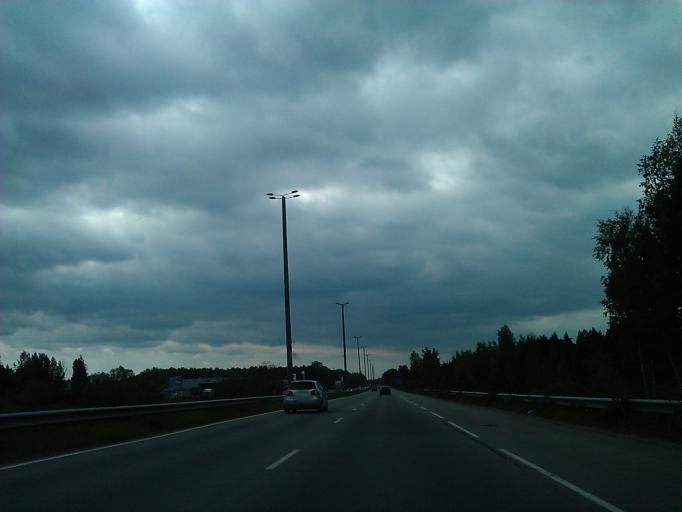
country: LV
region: Marupe
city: Marupe
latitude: 56.8860
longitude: 24.0743
